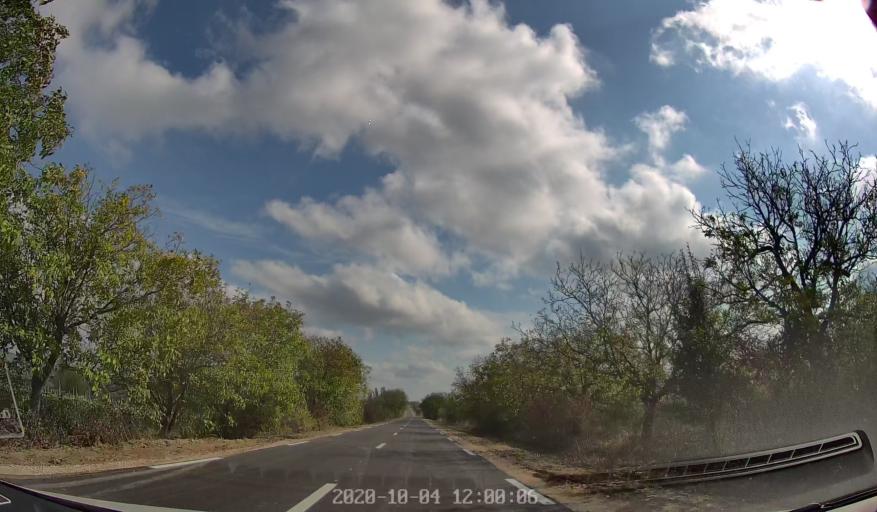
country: MD
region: Rezina
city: Saharna
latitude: 47.6317
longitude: 28.8649
